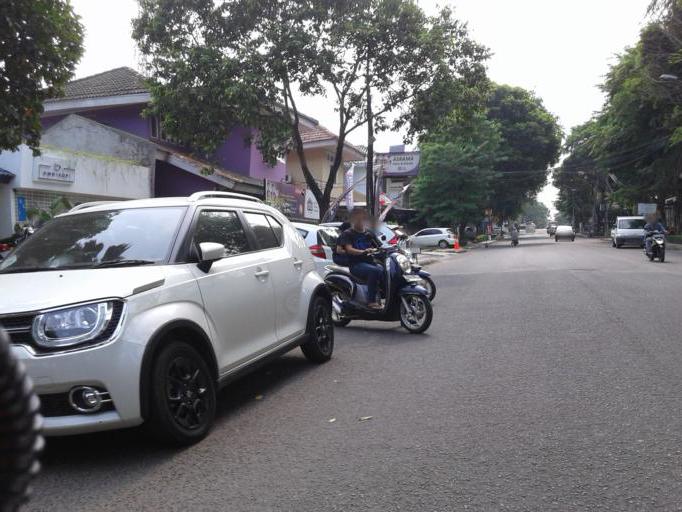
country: ID
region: Banten
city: South Tangerang
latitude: -6.2852
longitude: 106.7040
